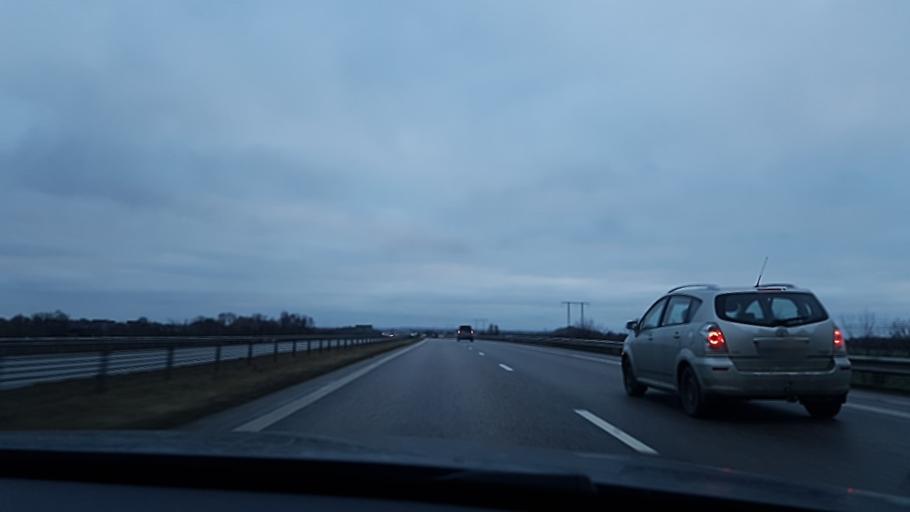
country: SE
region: Skane
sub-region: Astorps Kommun
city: Astorp
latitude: 56.1508
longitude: 12.9434
